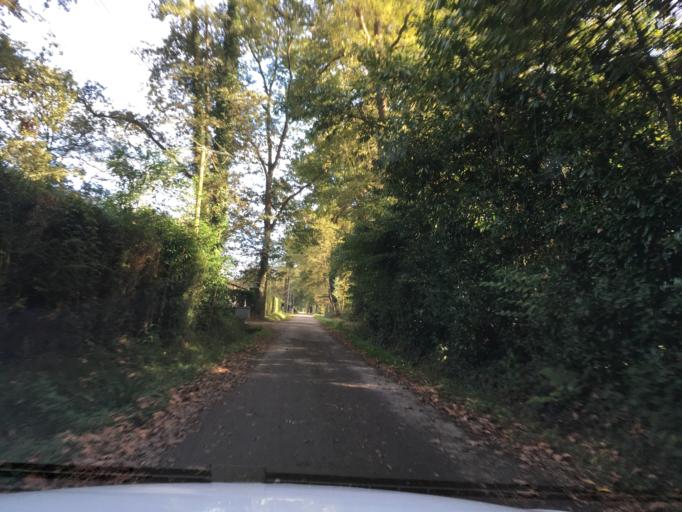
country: FR
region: Aquitaine
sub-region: Departement des Pyrenees-Atlantiques
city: Montardon
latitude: 43.3406
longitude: -0.3731
